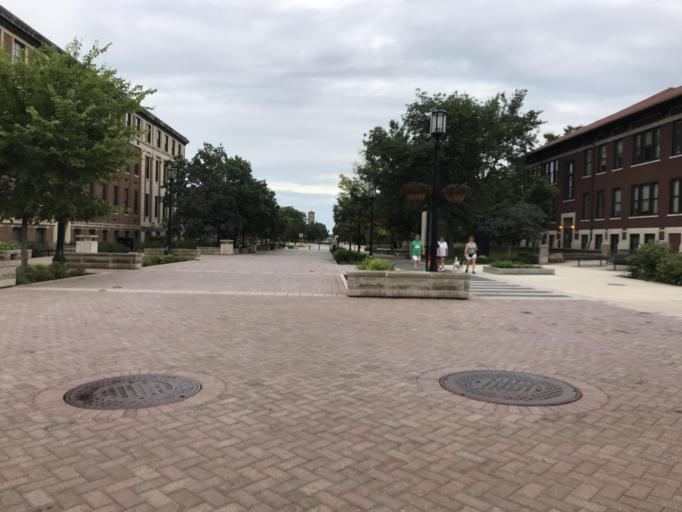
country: US
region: Indiana
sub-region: Tippecanoe County
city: West Lafayette
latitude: 40.4268
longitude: -86.9137
